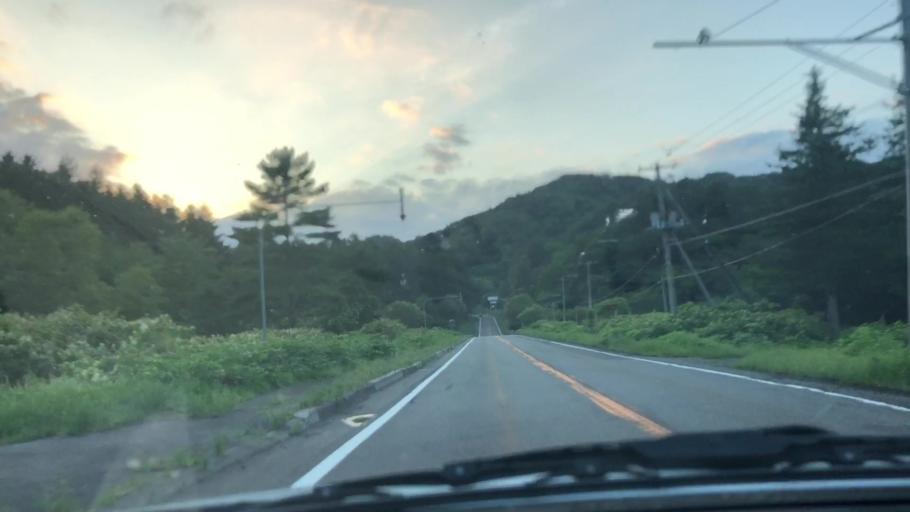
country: JP
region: Hokkaido
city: Chitose
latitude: 42.8704
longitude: 142.1538
